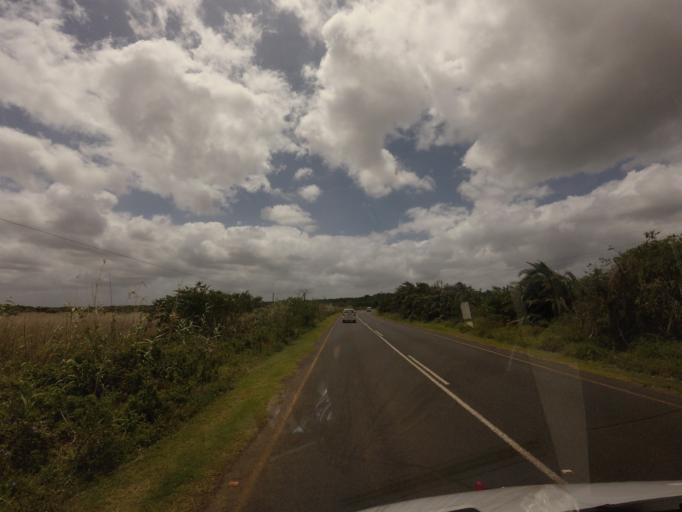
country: ZA
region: KwaZulu-Natal
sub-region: uMkhanyakude District Municipality
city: Mtubatuba
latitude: -28.3705
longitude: 32.4057
